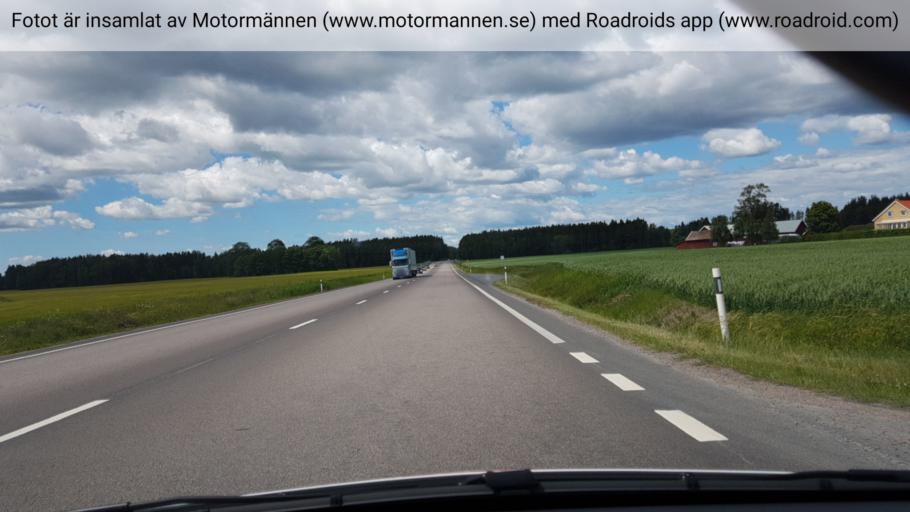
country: SE
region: Vaestra Goetaland
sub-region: Skara Kommun
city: Skara
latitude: 58.4106
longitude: 13.3798
